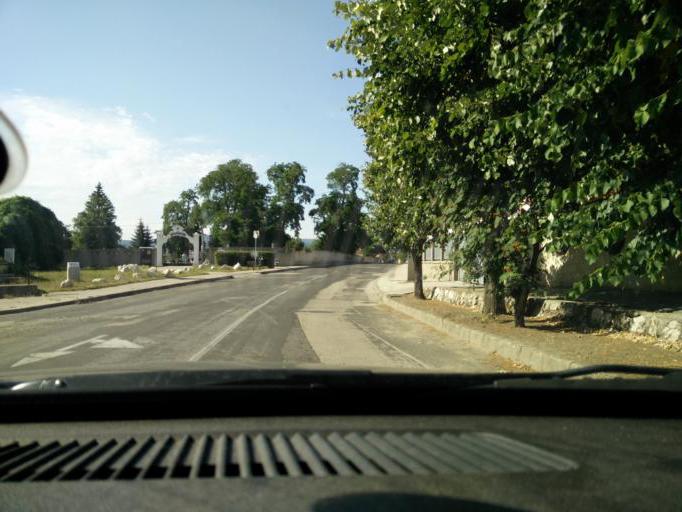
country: HU
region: Fejer
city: Szarliget
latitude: 47.5471
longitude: 18.4489
